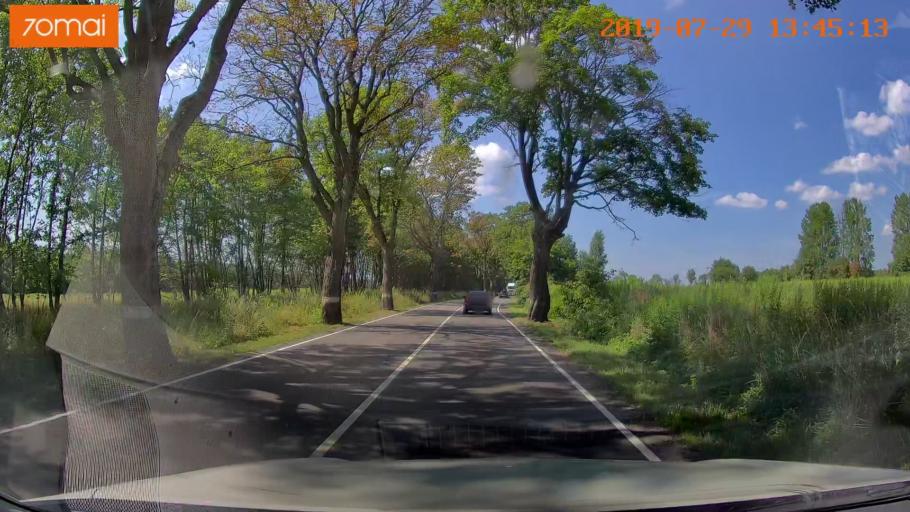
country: RU
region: Kaliningrad
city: Primorsk
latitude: 54.7393
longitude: 20.0773
